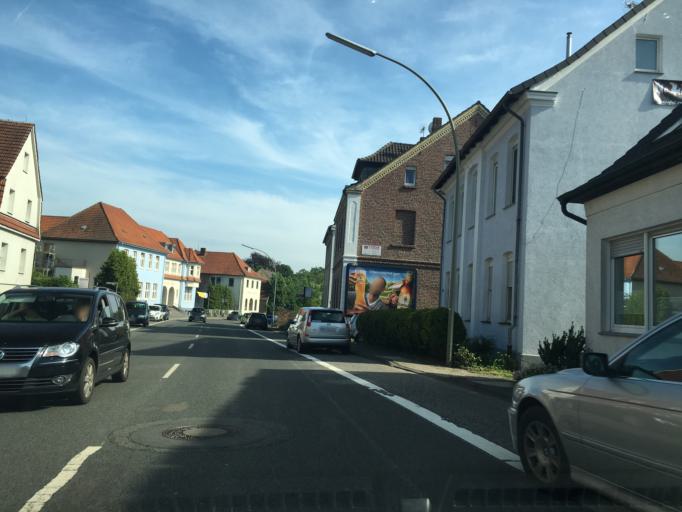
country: DE
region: North Rhine-Westphalia
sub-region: Regierungsbezirk Munster
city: Steinfurt
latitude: 52.1513
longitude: 7.3413
